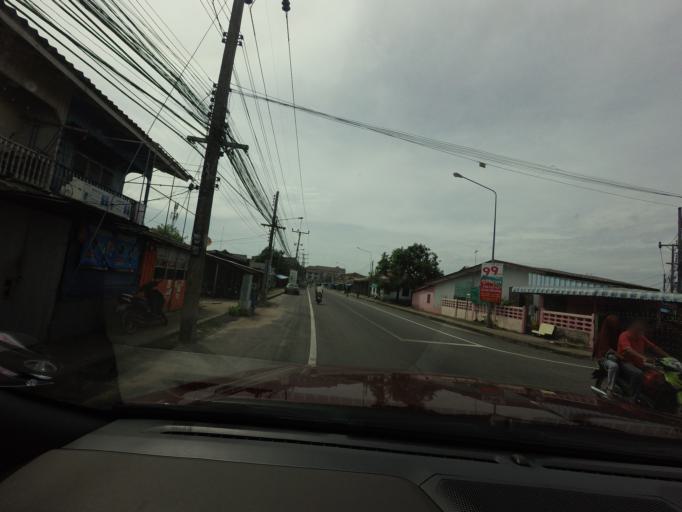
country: TH
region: Narathiwat
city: Tak Bai
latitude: 6.2375
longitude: 102.0875
